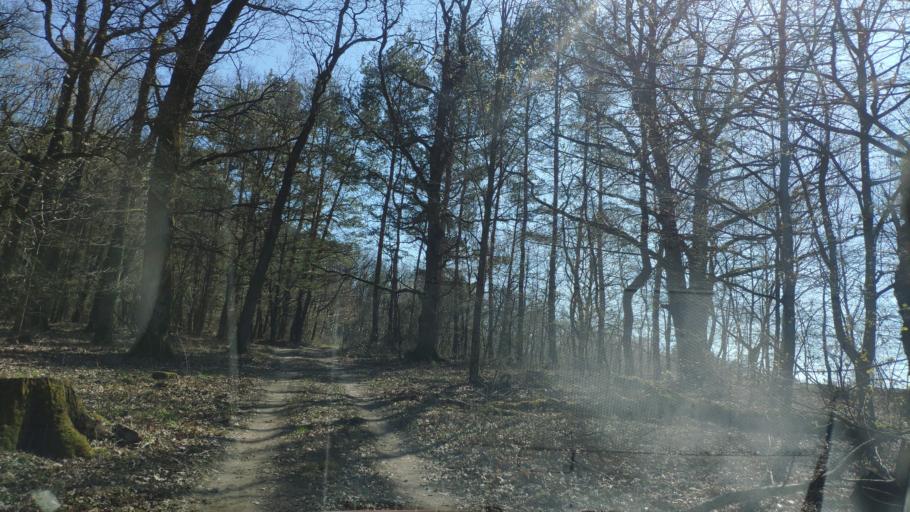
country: SK
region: Kosicky
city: Moldava nad Bodvou
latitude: 48.5643
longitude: 20.9304
